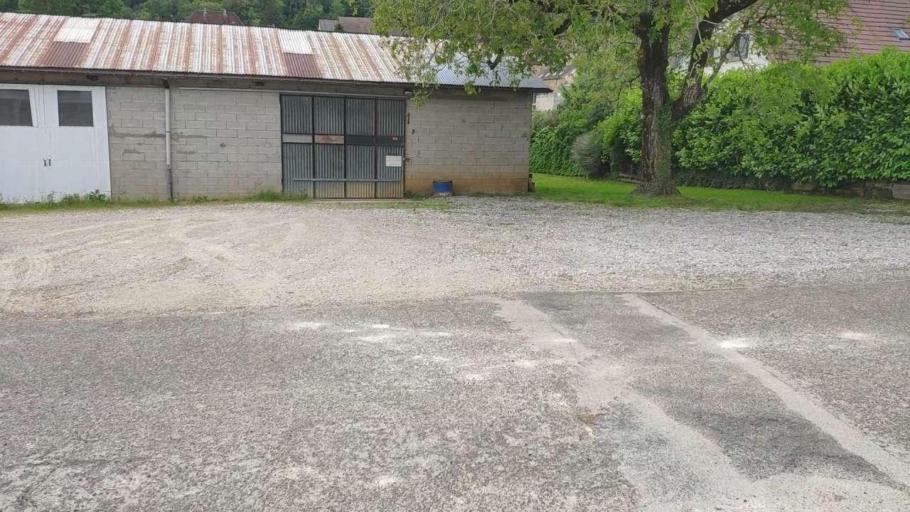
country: FR
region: Franche-Comte
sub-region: Departement du Jura
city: Perrigny
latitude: 46.7828
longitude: 5.5811
